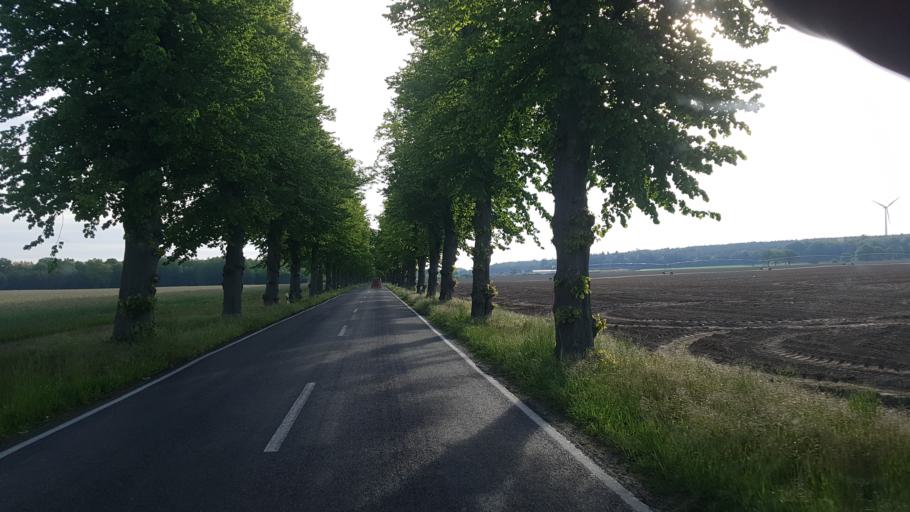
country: DE
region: Brandenburg
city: Dahme
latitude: 51.8947
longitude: 13.4758
